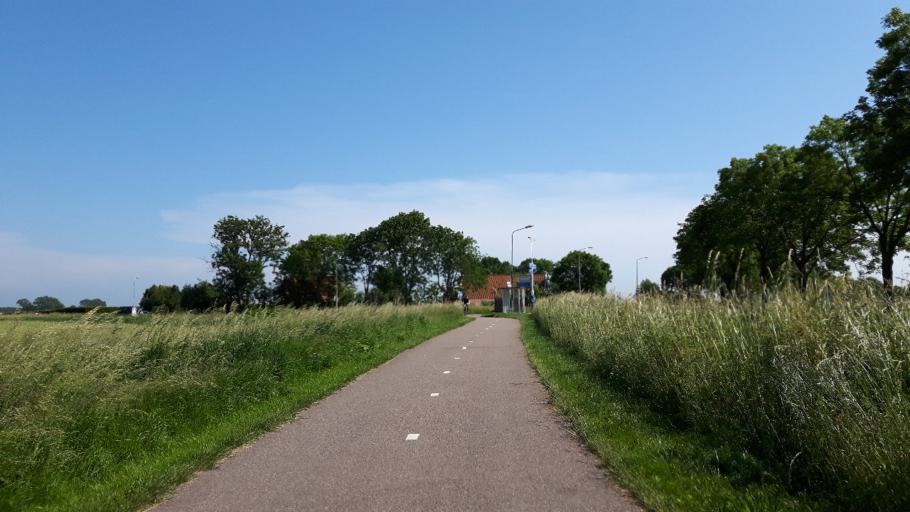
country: NL
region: Utrecht
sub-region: Stichtse Vecht
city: Vreeland
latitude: 52.2497
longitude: 5.0530
